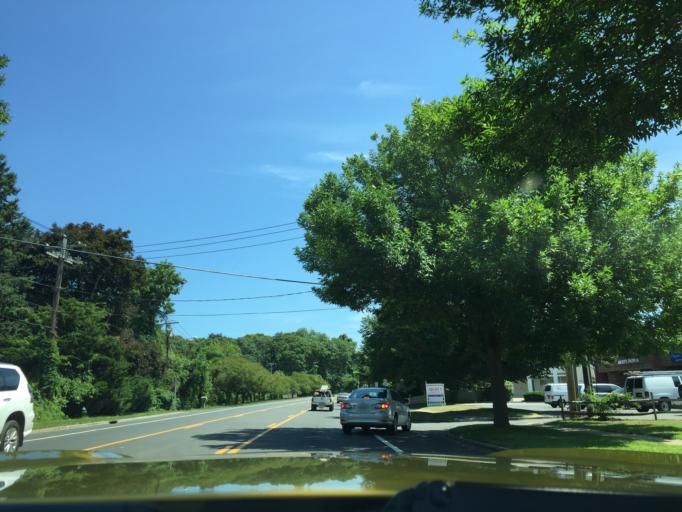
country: US
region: New York
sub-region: Suffolk County
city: Amagansett
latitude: 40.9690
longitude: -72.1604
